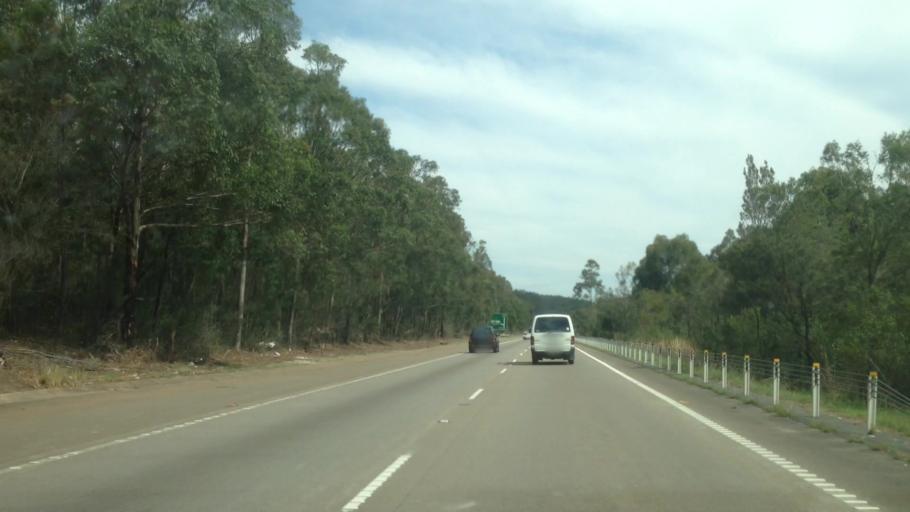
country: AU
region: New South Wales
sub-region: Lake Macquarie Shire
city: Fennell Bay
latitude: -32.9663
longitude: 151.5369
